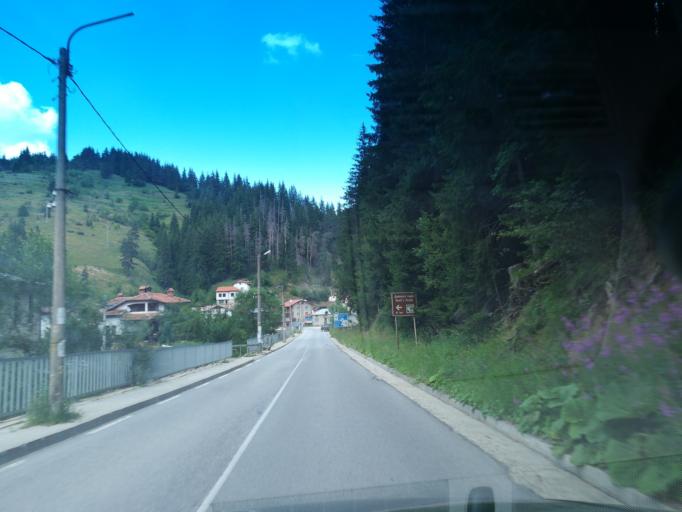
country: BG
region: Smolyan
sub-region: Obshtina Chepelare
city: Chepelare
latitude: 41.6617
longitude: 24.6343
